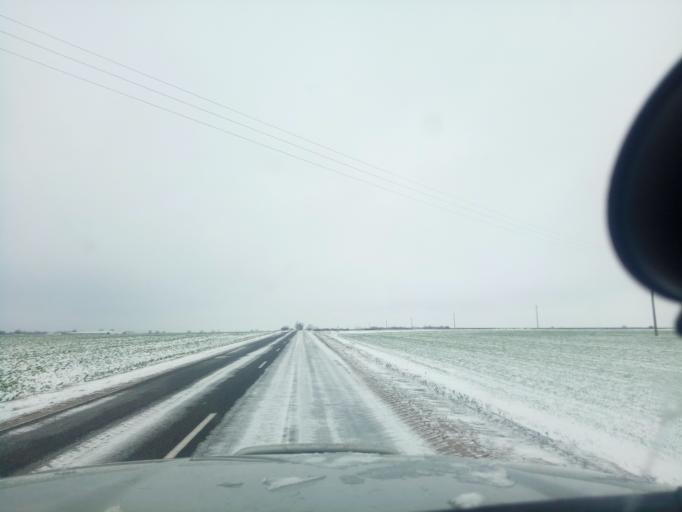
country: BY
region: Minsk
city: Klyetsk
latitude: 53.0515
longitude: 26.7592
